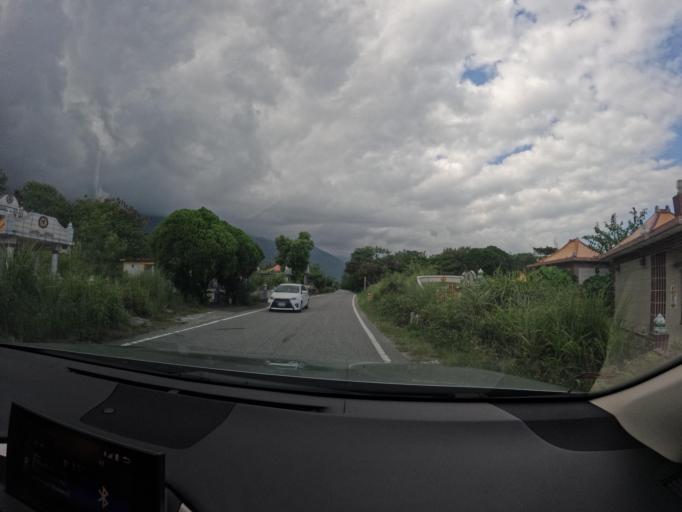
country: TW
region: Taiwan
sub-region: Hualien
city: Hualian
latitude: 24.0523
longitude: 121.6159
